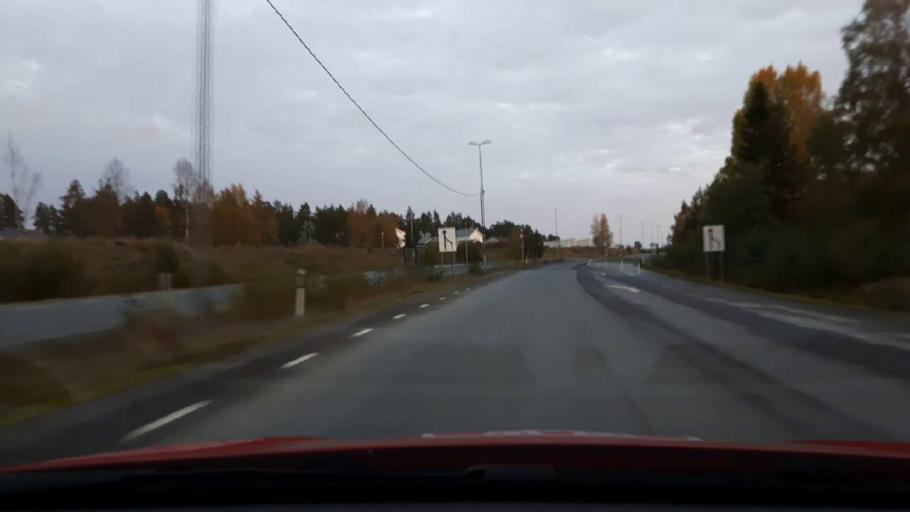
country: SE
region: Jaemtland
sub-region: OEstersunds Kommun
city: Ostersund
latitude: 63.1965
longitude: 14.6447
